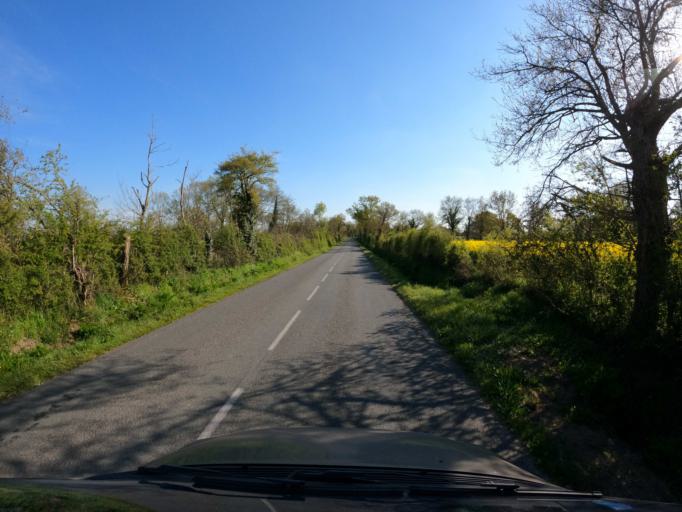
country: FR
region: Pays de la Loire
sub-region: Departement de la Vendee
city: Beaurepaire
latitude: 46.9186
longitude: -1.1222
